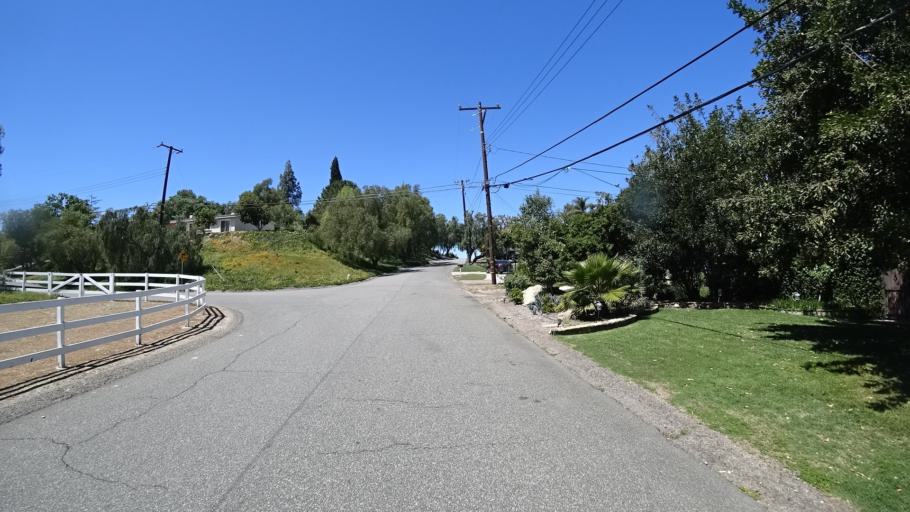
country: US
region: California
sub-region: Ventura County
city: Thousand Oaks
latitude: 34.1869
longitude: -118.8492
